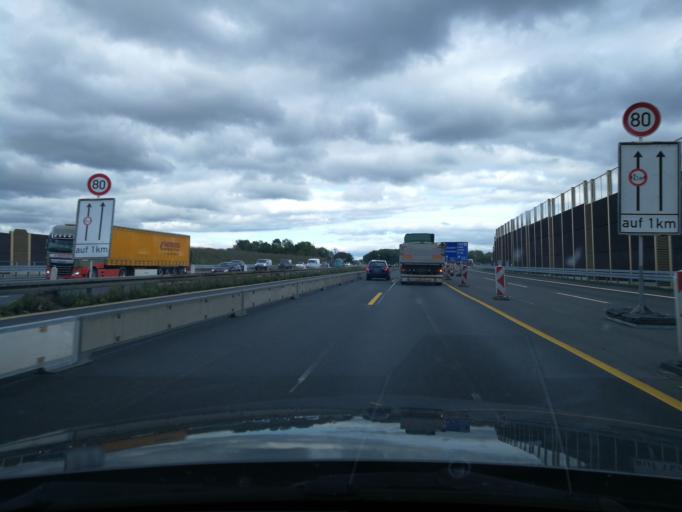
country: DE
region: North Rhine-Westphalia
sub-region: Regierungsbezirk Dusseldorf
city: Korschenbroich
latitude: 51.2427
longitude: 6.4768
